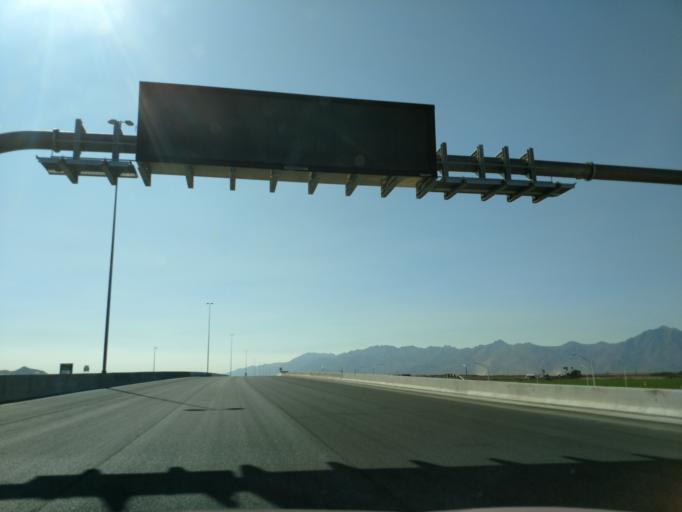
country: US
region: Arizona
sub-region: Maricopa County
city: Laveen
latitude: 33.3793
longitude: -112.1900
